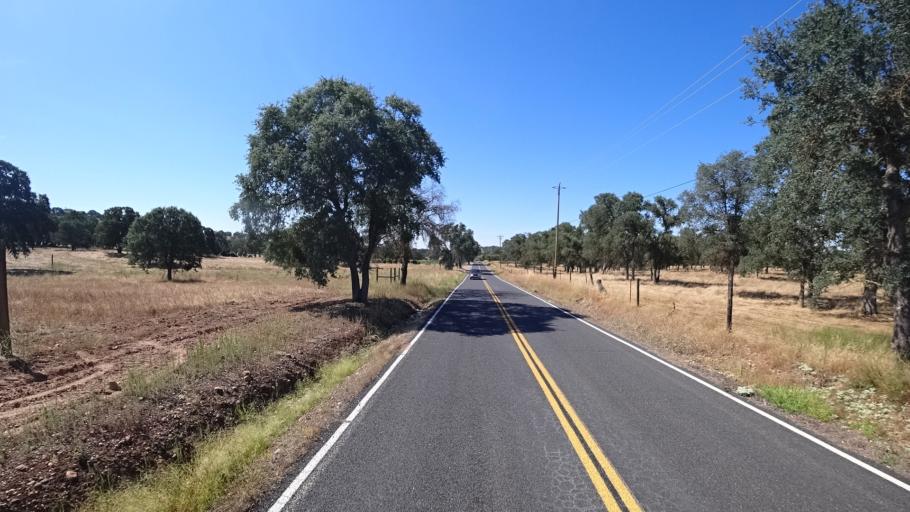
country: US
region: California
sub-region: Calaveras County
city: Rancho Calaveras
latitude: 38.1187
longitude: -120.9265
